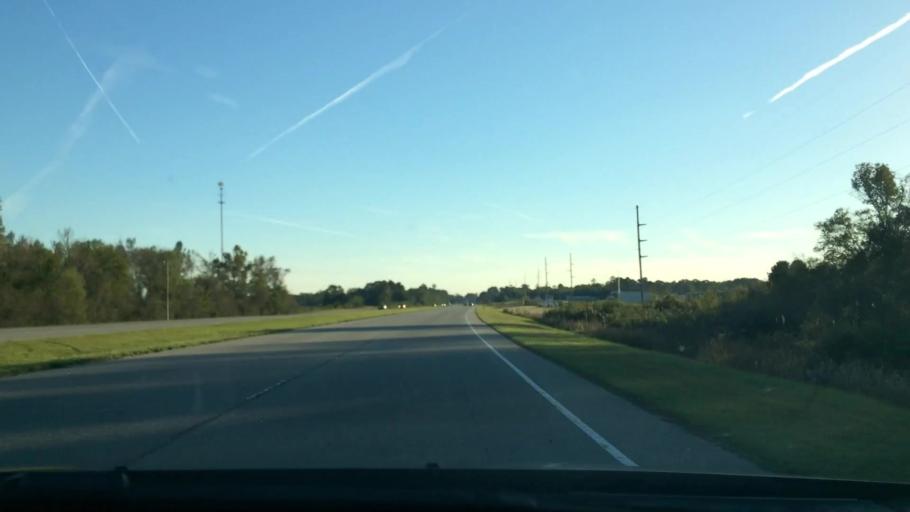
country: US
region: North Carolina
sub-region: Pitt County
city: Grifton
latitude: 35.3774
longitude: -77.4518
